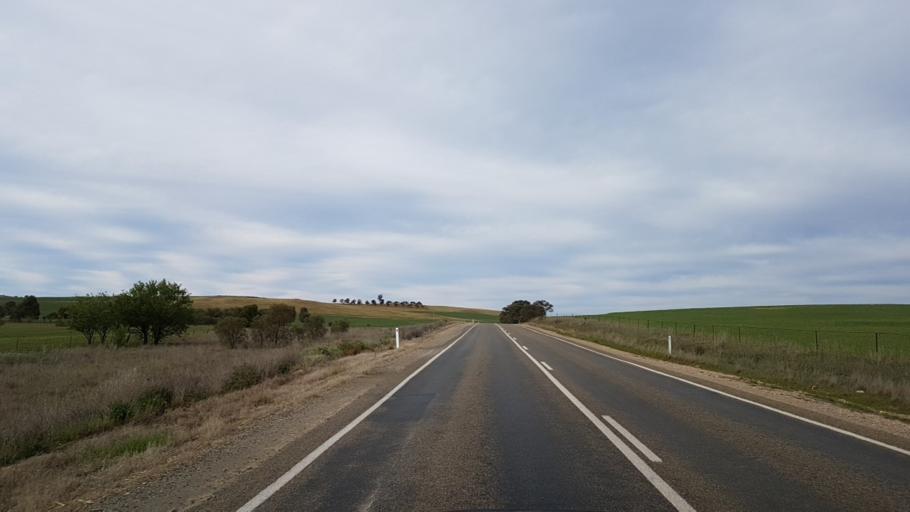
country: AU
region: South Australia
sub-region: Northern Areas
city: Jamestown
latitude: -33.2094
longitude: 138.4270
